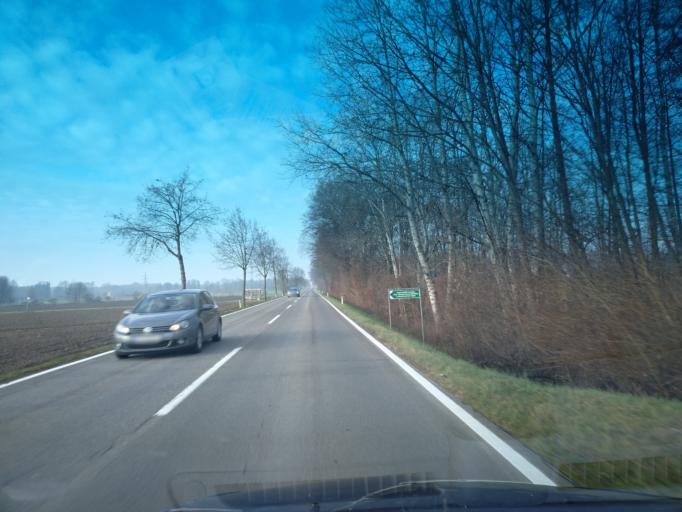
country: AT
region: Styria
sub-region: Politischer Bezirk Leibnitz
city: Strass in Steiermark
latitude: 46.7181
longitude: 15.6274
